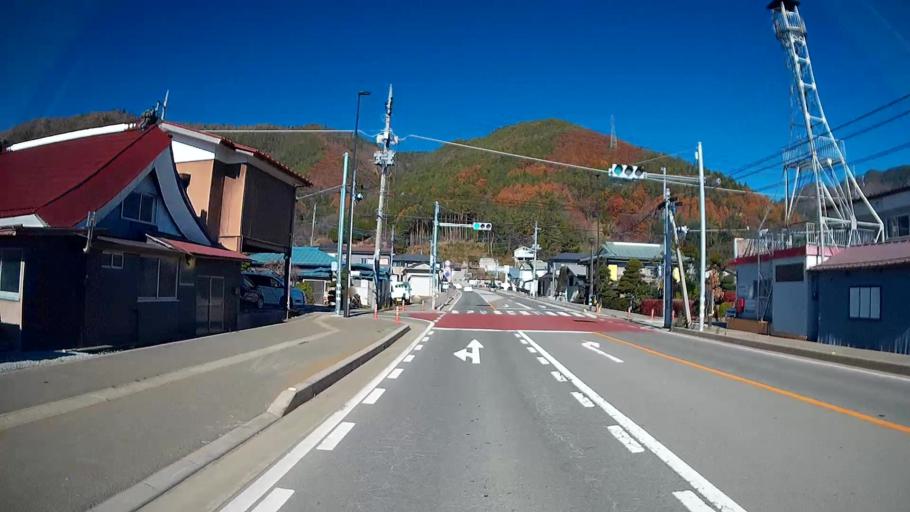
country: JP
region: Yamanashi
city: Fujikawaguchiko
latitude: 35.4976
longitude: 138.7918
